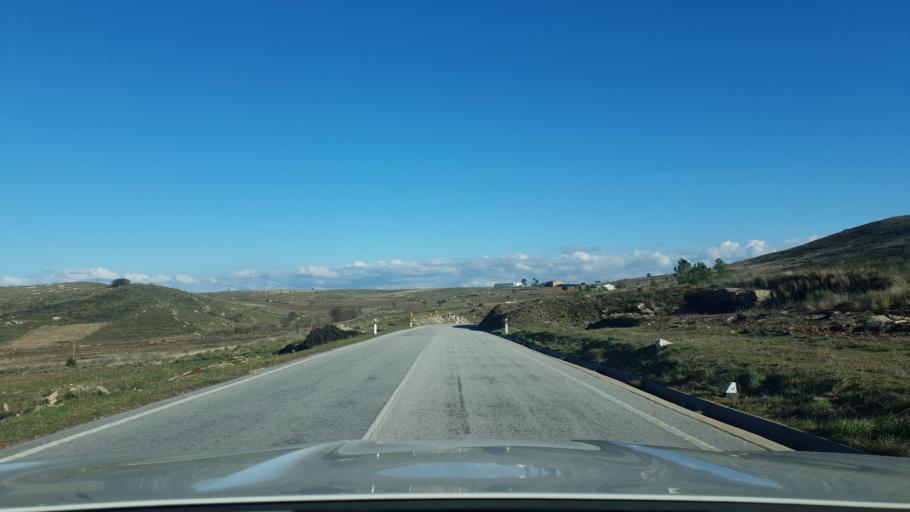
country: PT
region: Braganca
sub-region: Freixo de Espada A Cinta
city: Freixo de Espada a Cinta
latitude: 41.1812
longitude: -6.8047
